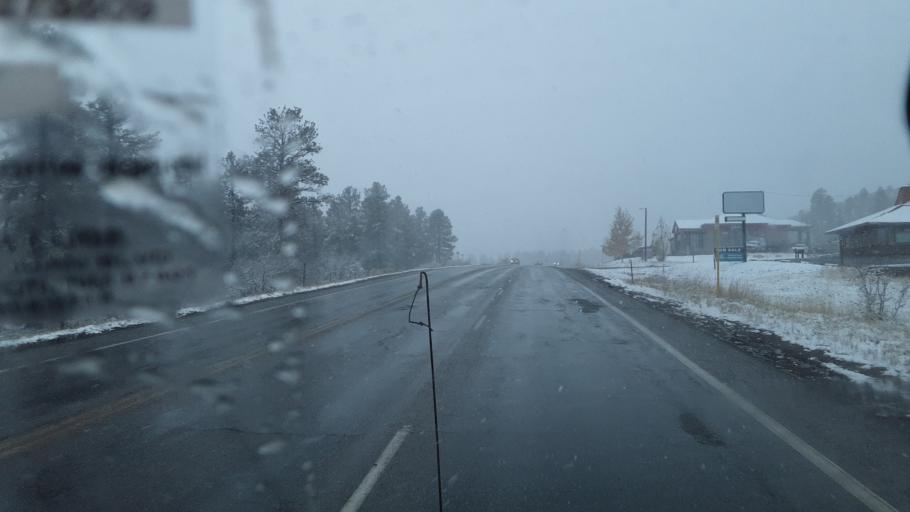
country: US
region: Colorado
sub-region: Archuleta County
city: Pagosa Springs
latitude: 37.2718
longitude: -107.0395
